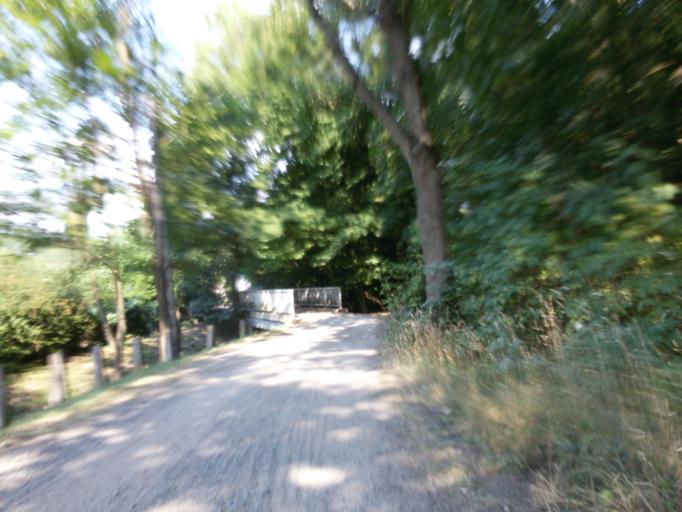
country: CZ
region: South Moravian
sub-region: Mesto Brno
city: Mokra Hora
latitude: 49.2408
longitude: 16.5921
